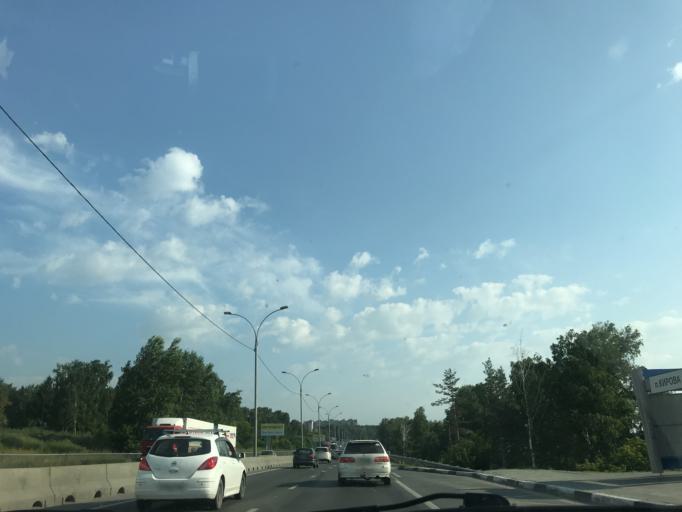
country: RU
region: Novosibirsk
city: Akademgorodok
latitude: 54.8145
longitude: 83.0891
